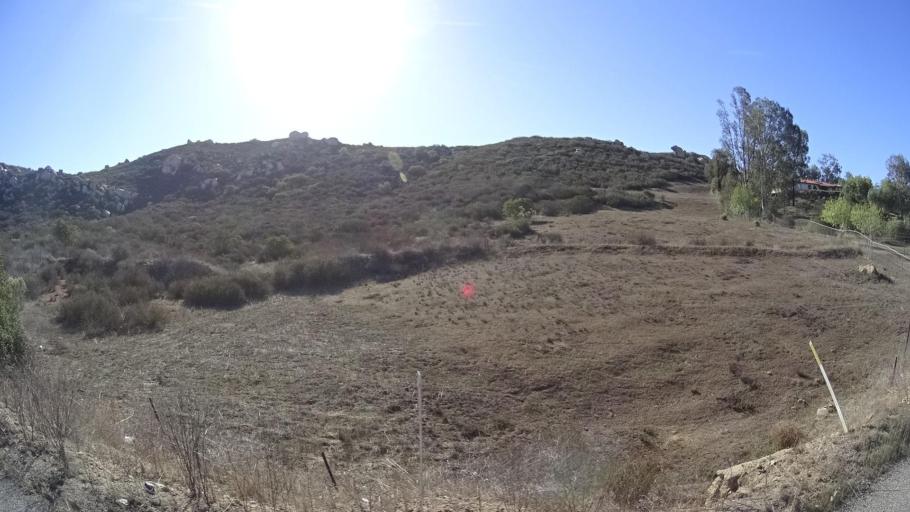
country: US
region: California
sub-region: San Diego County
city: Jamul
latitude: 32.6661
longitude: -116.7867
